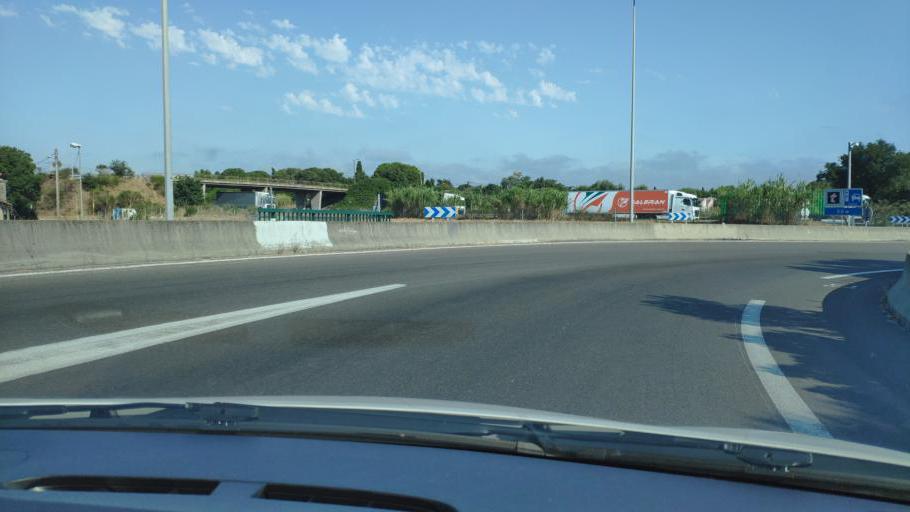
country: FR
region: Provence-Alpes-Cote d'Azur
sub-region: Departement des Bouches-du-Rhone
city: Salon-de-Provence
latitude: 43.6255
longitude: 5.1010
